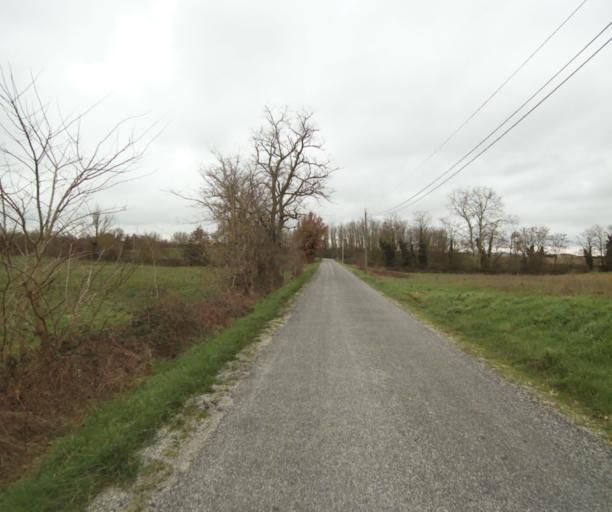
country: FR
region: Midi-Pyrenees
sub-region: Departement de l'Ariege
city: Mazeres
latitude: 43.2360
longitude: 1.6814
